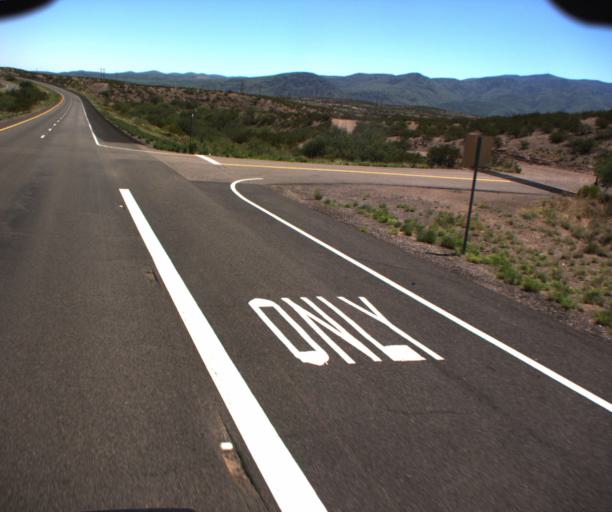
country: US
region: Arizona
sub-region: Greenlee County
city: Clifton
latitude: 32.9982
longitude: -109.2758
